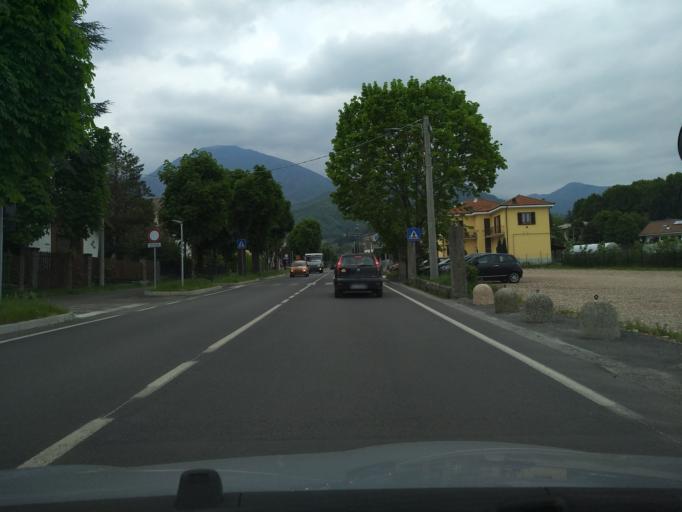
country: IT
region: Piedmont
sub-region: Provincia di Torino
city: Luserna
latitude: 44.8171
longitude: 7.2385
